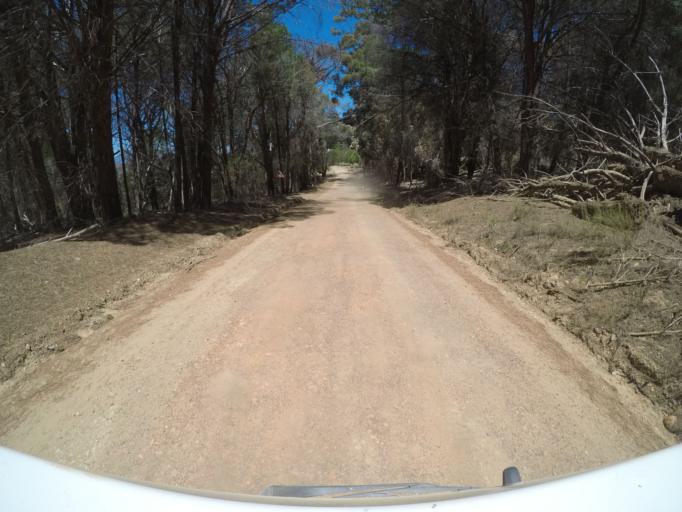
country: ZA
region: Western Cape
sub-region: Overberg District Municipality
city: Grabouw
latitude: -34.1634
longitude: 19.2244
